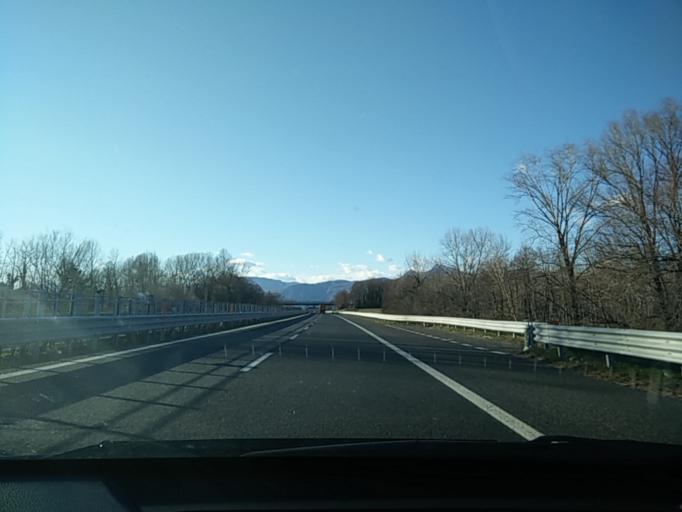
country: IT
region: Friuli Venezia Giulia
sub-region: Provincia di Udine
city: Collofedo di Monte Albano
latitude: 46.1807
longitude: 13.1326
